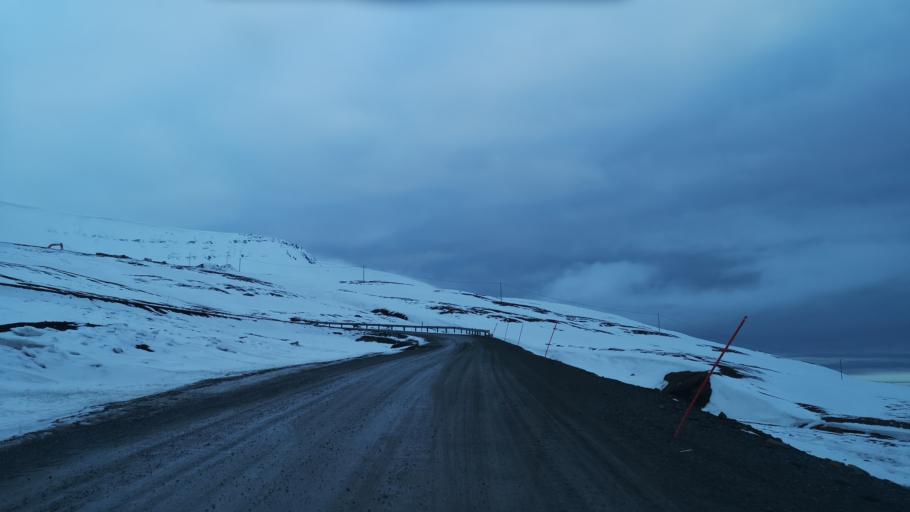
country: SJ
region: Svalbard
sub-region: Spitsbergen
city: Longyearbyen
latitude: 78.2379
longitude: 15.5004
